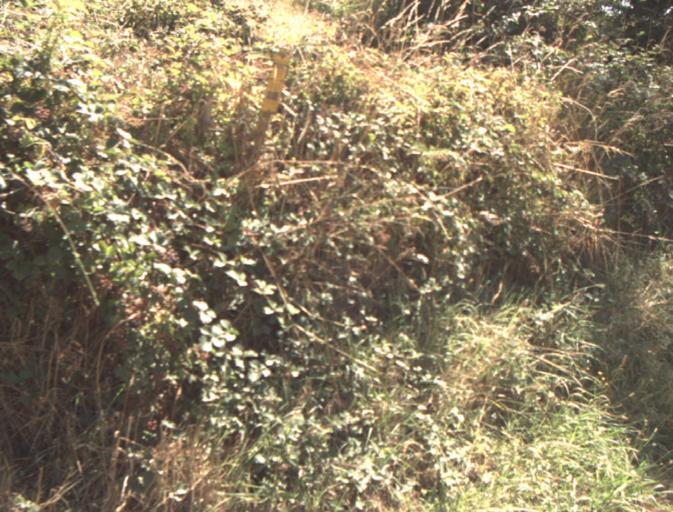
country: AU
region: Tasmania
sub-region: Launceston
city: Mayfield
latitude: -41.2570
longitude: 147.1699
